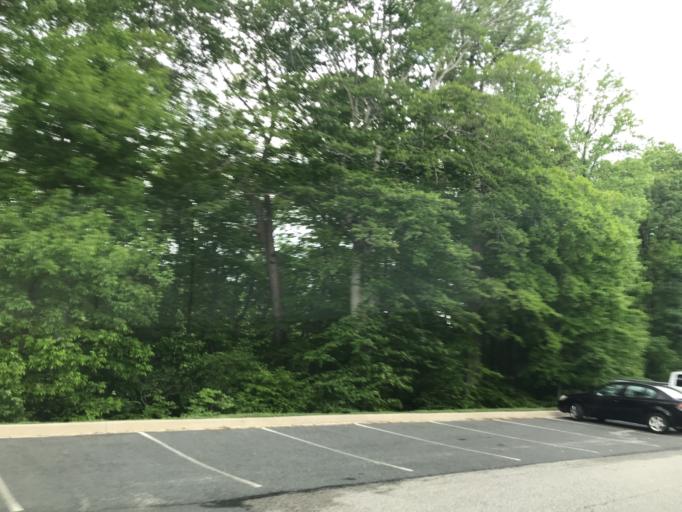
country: US
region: Maryland
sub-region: Harford County
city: North Bel Air
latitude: 39.5306
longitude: -76.3632
